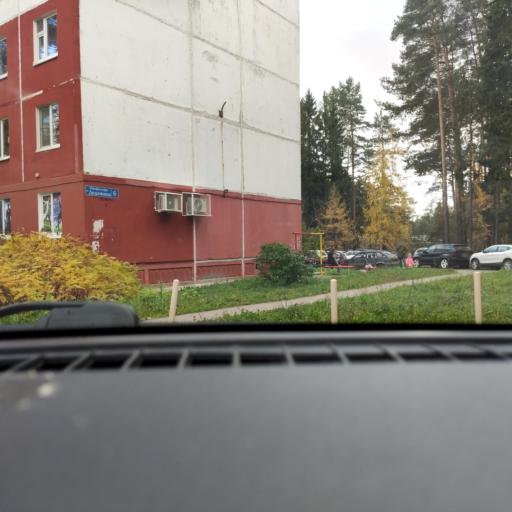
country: RU
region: Perm
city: Perm
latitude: 58.0498
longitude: 56.2146
